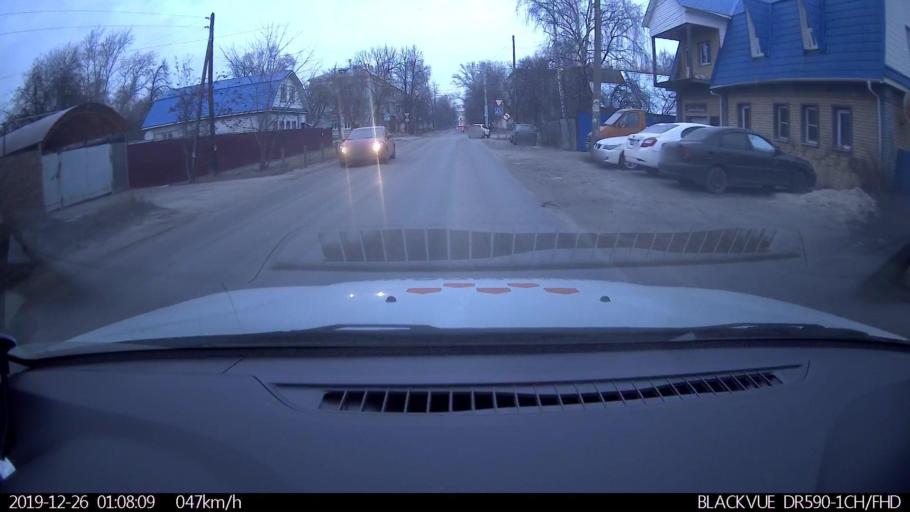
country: RU
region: Nizjnij Novgorod
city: Nizhniy Novgorod
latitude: 56.2868
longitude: 43.9131
